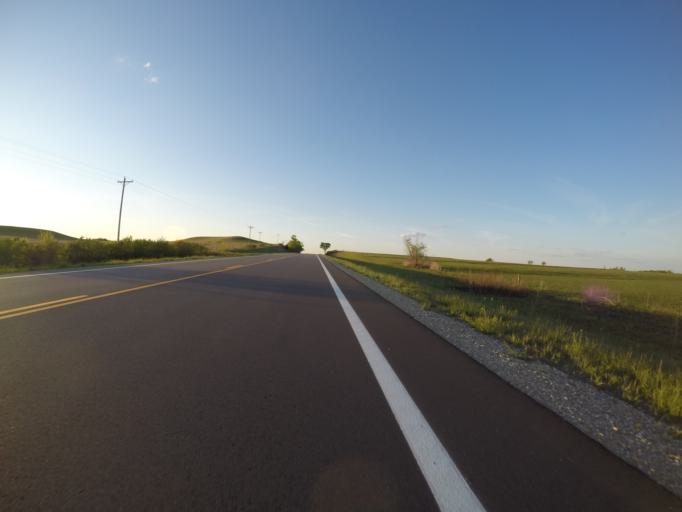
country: US
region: Kansas
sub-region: Pottawatomie County
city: Westmoreland
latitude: 39.3741
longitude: -96.5198
